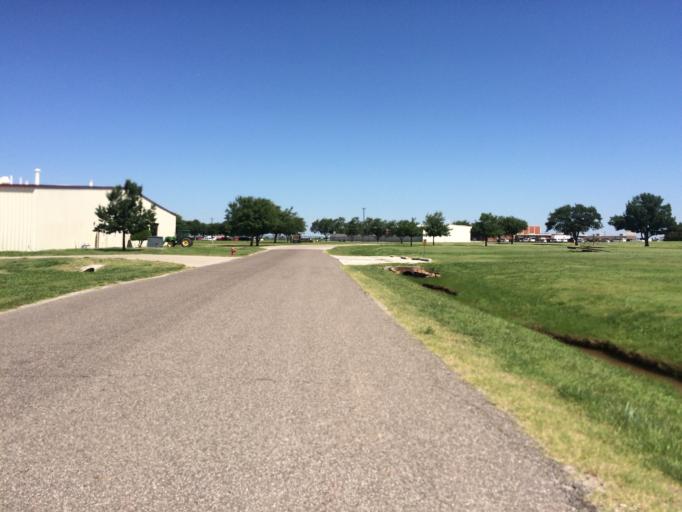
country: US
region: Oklahoma
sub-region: Cleveland County
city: Norman
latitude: 35.2398
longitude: -97.4655
